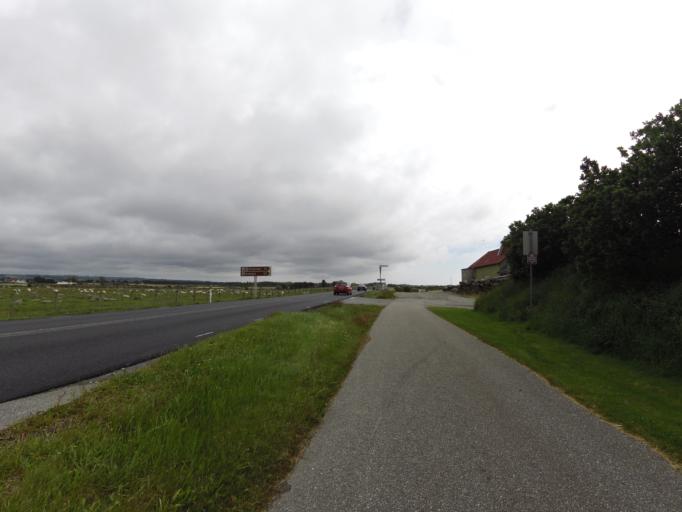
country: NO
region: Rogaland
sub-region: Ha
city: Naerbo
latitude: 58.6381
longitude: 5.6080
